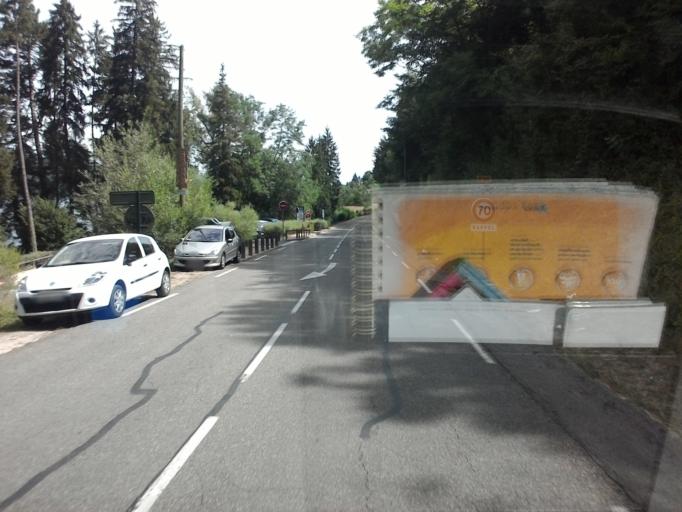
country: FR
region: Rhone-Alpes
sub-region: Departement de l'Isere
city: Charavines
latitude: 45.4411
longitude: 5.5263
